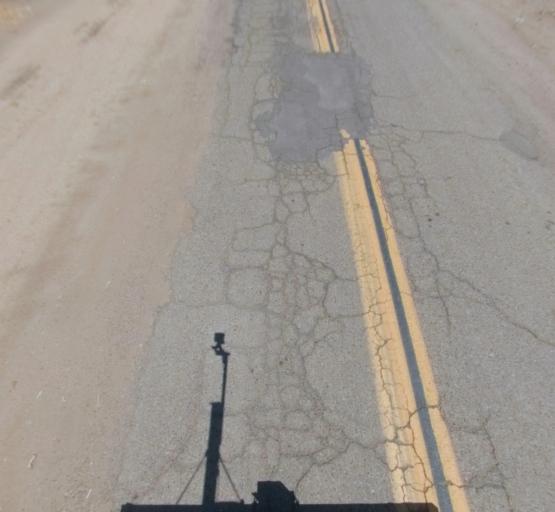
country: US
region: California
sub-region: Madera County
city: Chowchilla
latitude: 37.0909
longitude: -120.3651
